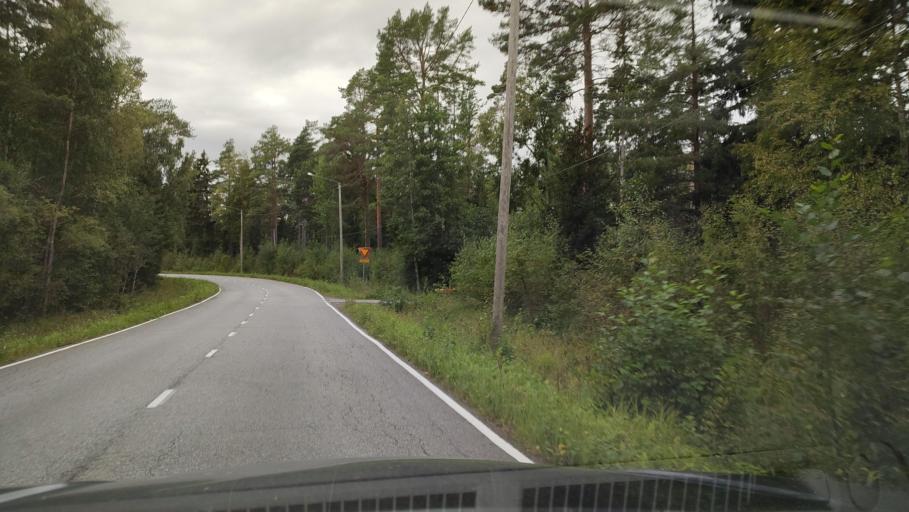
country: FI
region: Ostrobothnia
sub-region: Sydosterbotten
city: Kristinestad
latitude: 62.2639
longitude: 21.3533
